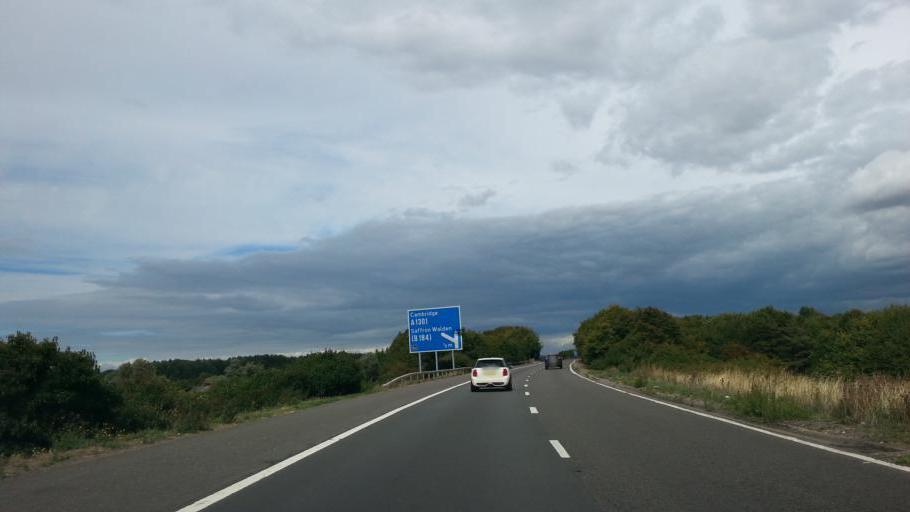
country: GB
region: England
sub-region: Cambridgeshire
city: Duxford
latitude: 52.0634
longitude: 0.1838
